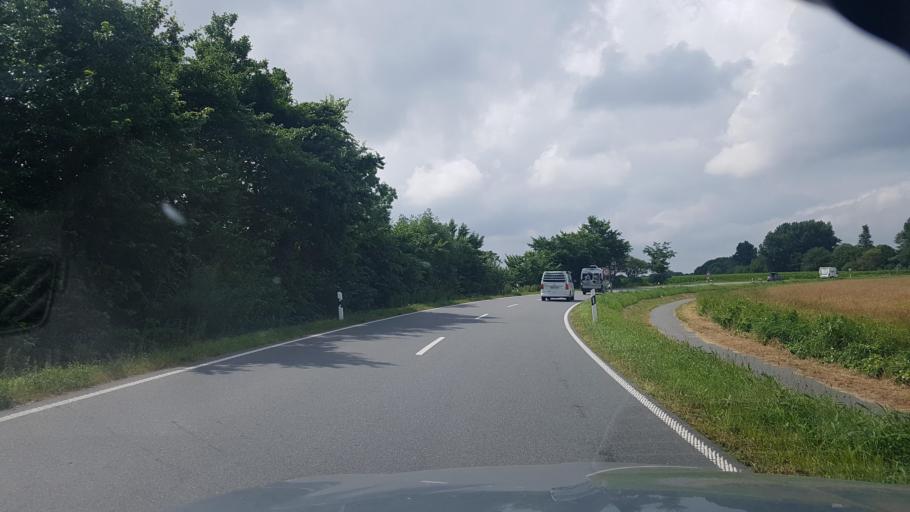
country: DE
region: Schleswig-Holstein
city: Elisabeth-Sophien-Koog
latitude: 54.4998
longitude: 8.9395
